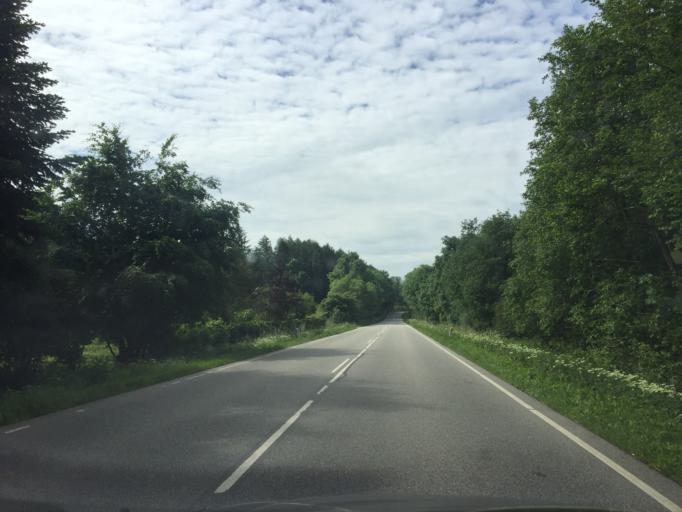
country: DK
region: South Denmark
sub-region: Nyborg Kommune
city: Ullerslev
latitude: 55.2350
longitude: 10.6489
